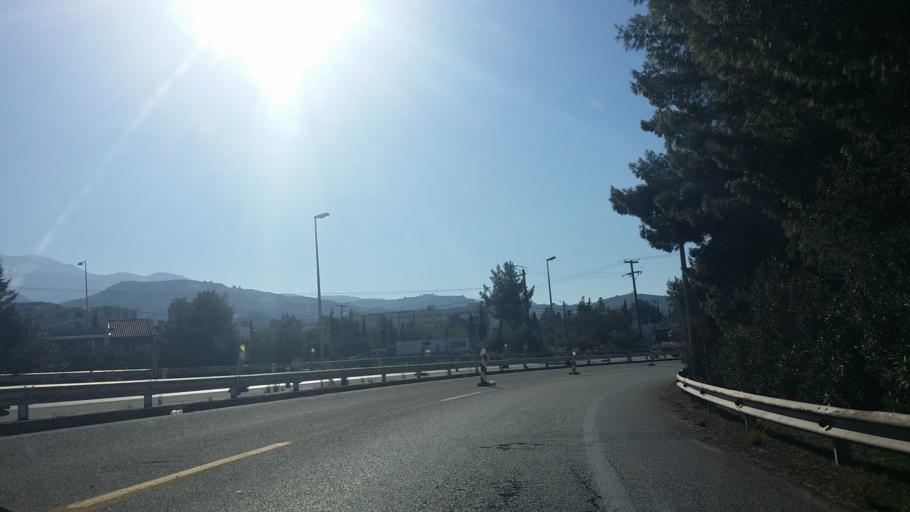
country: GR
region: West Greece
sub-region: Nomos Achaias
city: Rio
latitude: 38.2974
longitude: 21.7933
